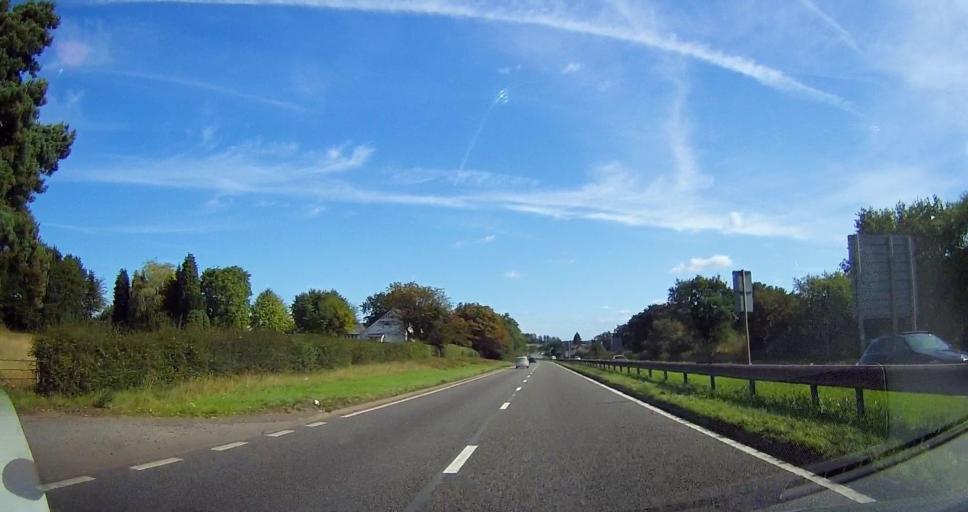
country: GB
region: England
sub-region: Staffordshire
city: Shenstone
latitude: 52.6561
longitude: -1.8778
